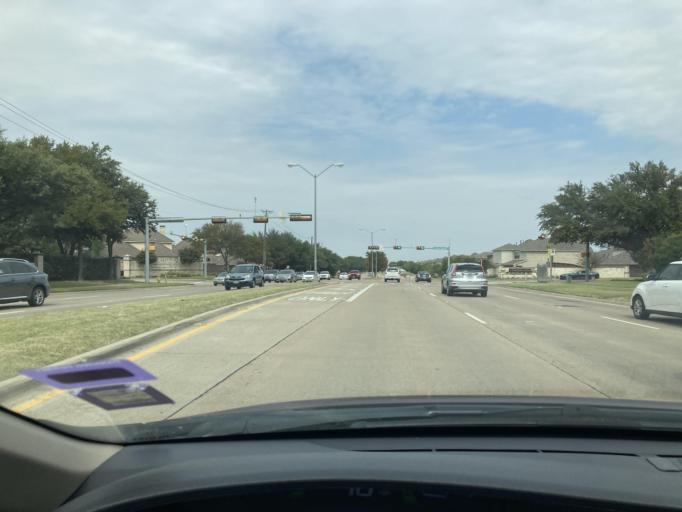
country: US
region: Texas
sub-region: Dallas County
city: Addison
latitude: 33.0350
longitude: -96.7946
